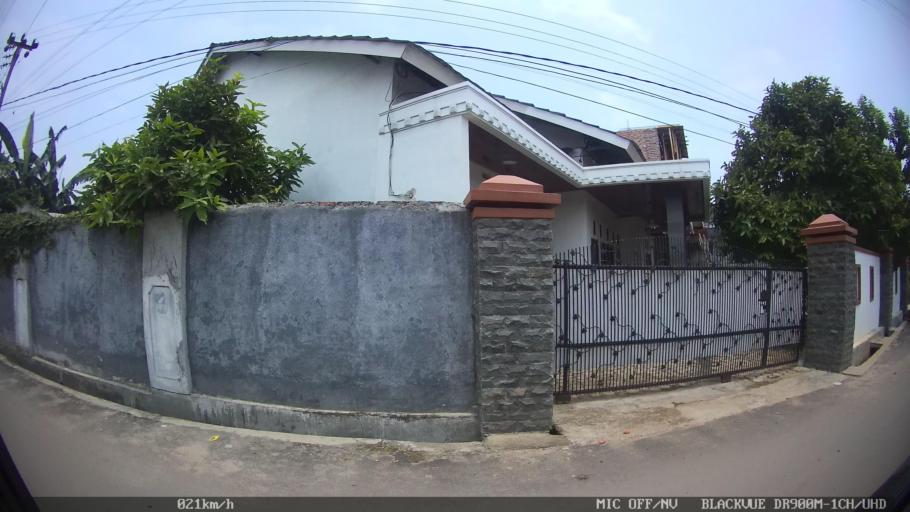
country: ID
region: Lampung
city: Bandarlampung
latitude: -5.4180
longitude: 105.2753
